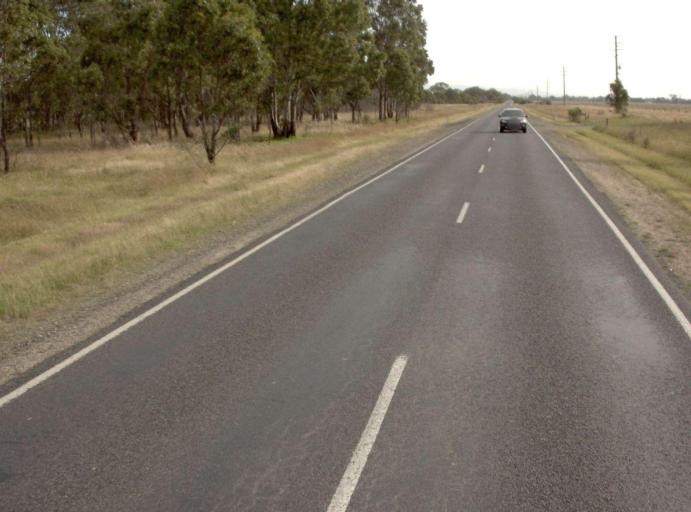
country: AU
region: Victoria
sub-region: Latrobe
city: Traralgon
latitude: -38.0771
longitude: 146.6105
